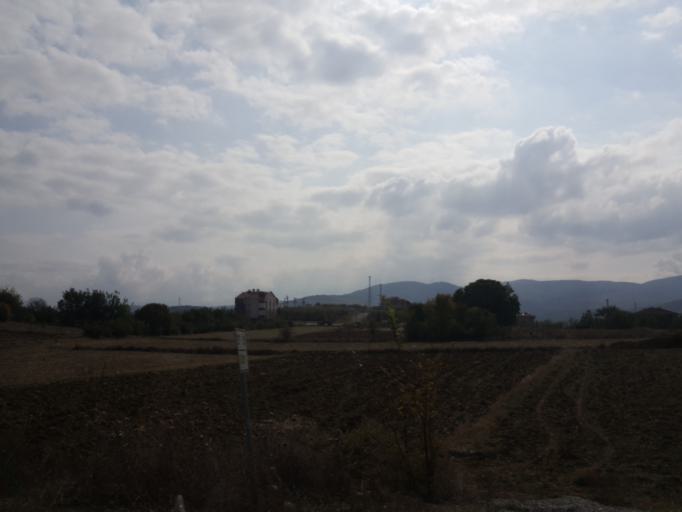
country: TR
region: Sinop
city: Sarayduzu
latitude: 41.3332
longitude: 34.8536
